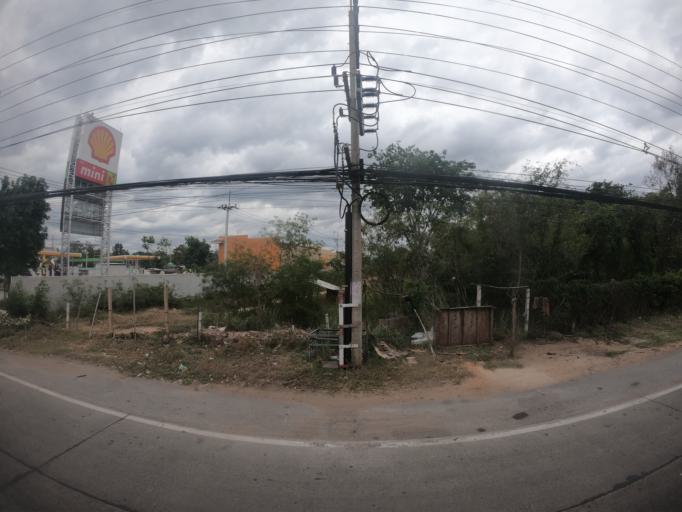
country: TH
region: Nakhon Ratchasima
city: Nakhon Ratchasima
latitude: 14.9140
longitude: 102.1501
